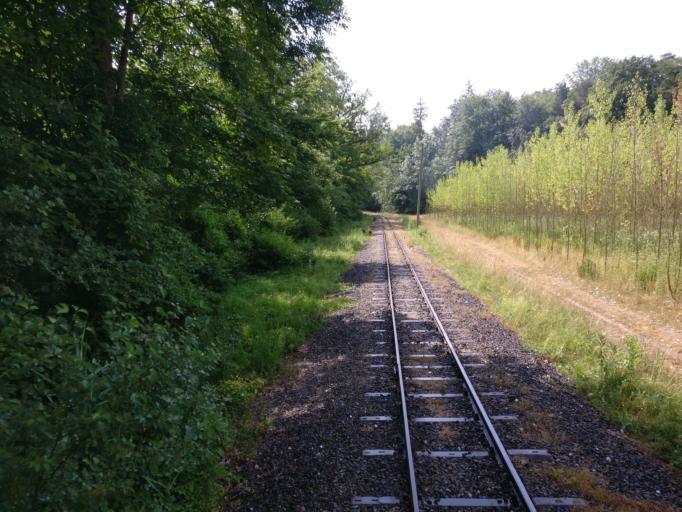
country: AT
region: Upper Austria
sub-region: Politischer Bezirk Steyr-Land
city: Garsten
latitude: 48.0456
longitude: 14.3690
